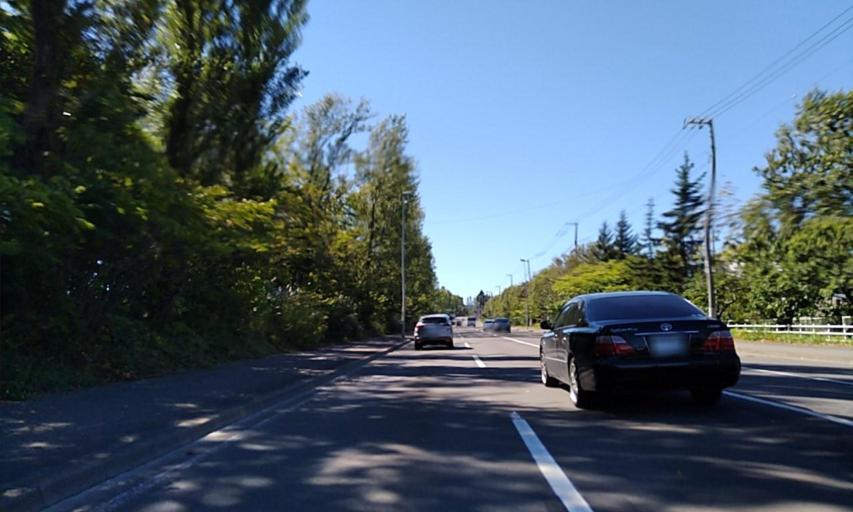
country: JP
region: Hokkaido
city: Sapporo
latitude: 43.0073
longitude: 141.3981
